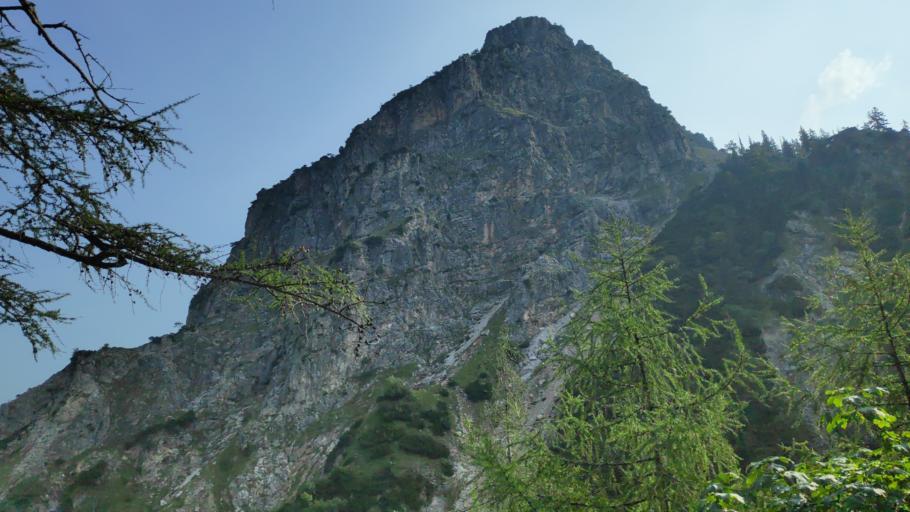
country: DE
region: Bavaria
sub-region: Upper Bavaria
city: Staudach-Egerndach
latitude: 47.7594
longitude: 12.5395
